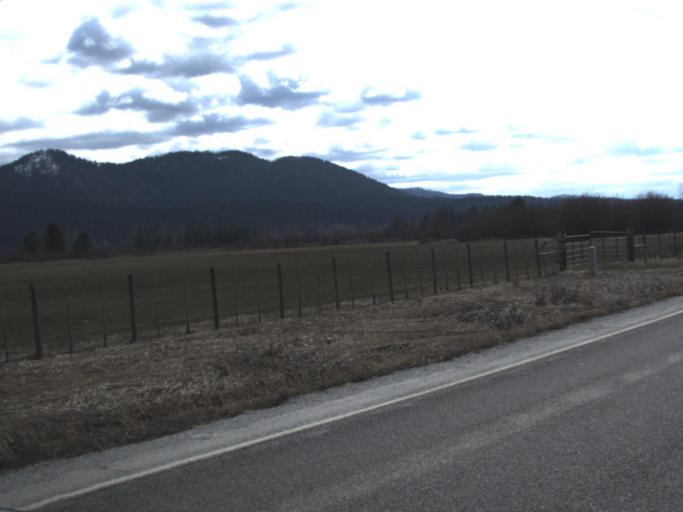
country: US
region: Washington
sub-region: Pend Oreille County
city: Newport
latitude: 48.3831
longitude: -117.3096
